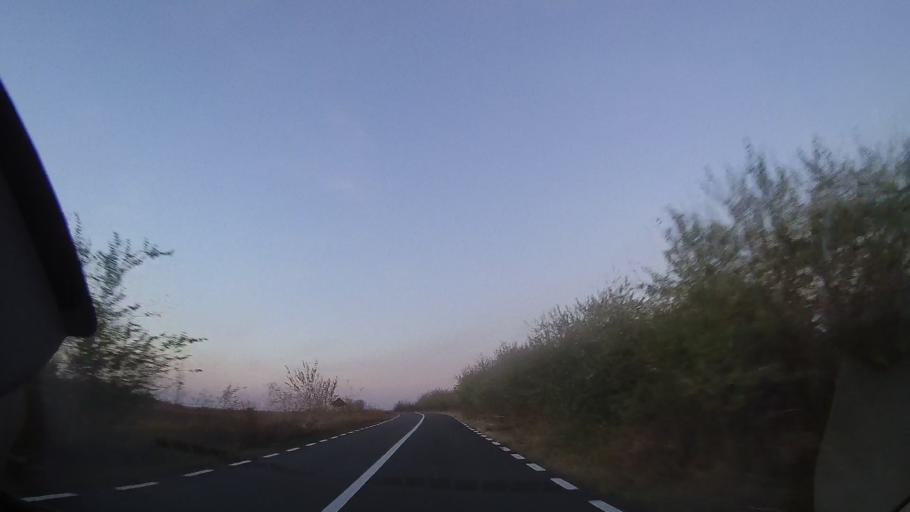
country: RO
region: Constanta
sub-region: Comuna Cobadin
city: Cobadin
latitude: 44.0343
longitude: 28.2601
